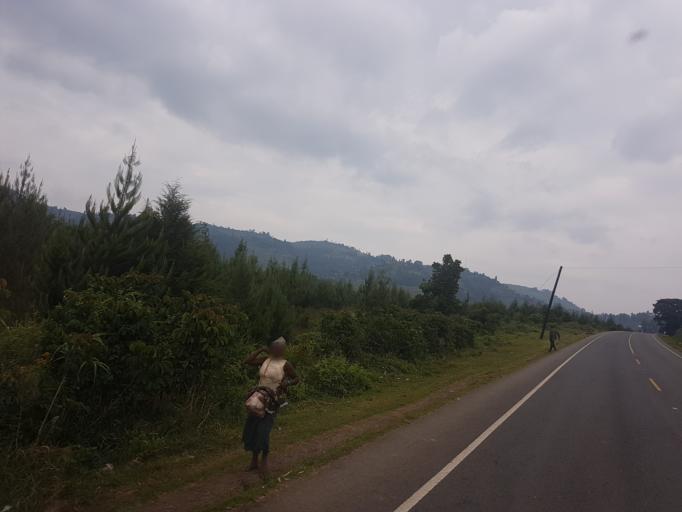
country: UG
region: Western Region
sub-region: Kisoro District
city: Kisoro
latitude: -1.2104
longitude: 29.8254
